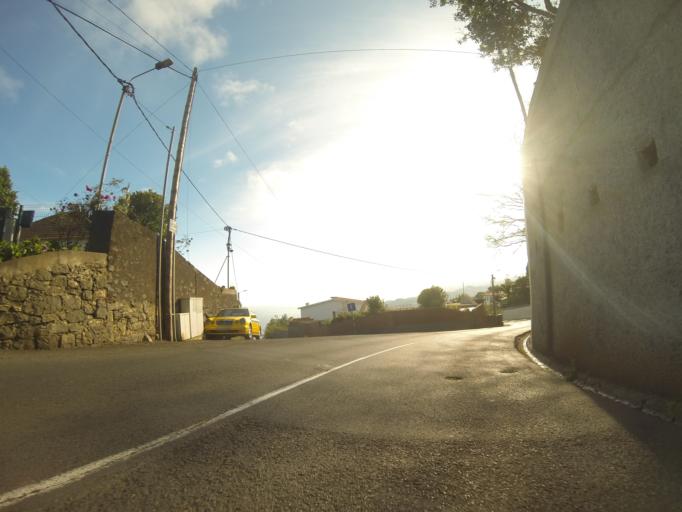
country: PT
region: Madeira
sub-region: Funchal
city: Nossa Senhora do Monte
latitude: 32.6602
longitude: -16.8790
